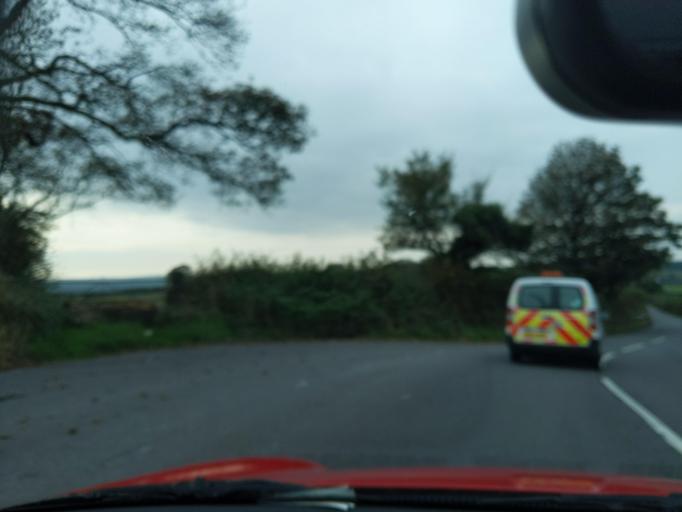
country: GB
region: England
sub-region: Devon
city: Great Torrington
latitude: 50.8663
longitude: -4.0706
